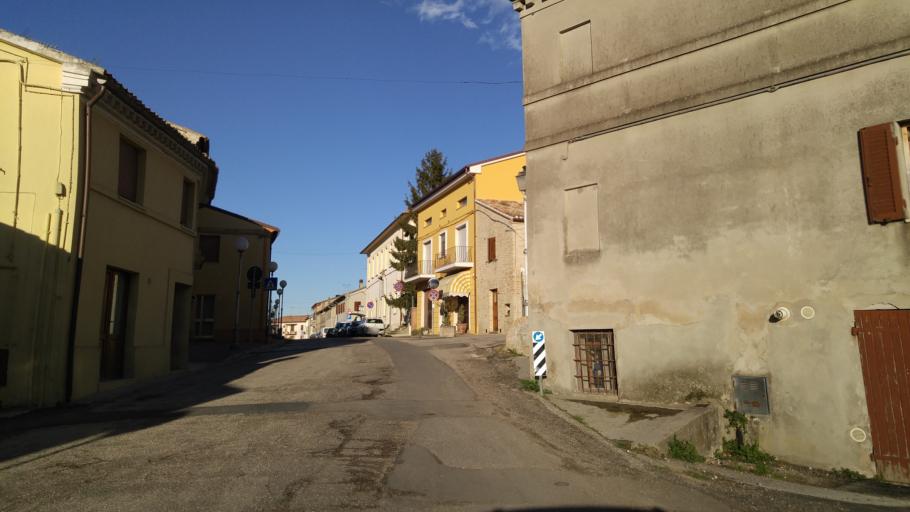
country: IT
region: The Marches
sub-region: Provincia di Pesaro e Urbino
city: Bellocchi
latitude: 43.7524
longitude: 13.0127
